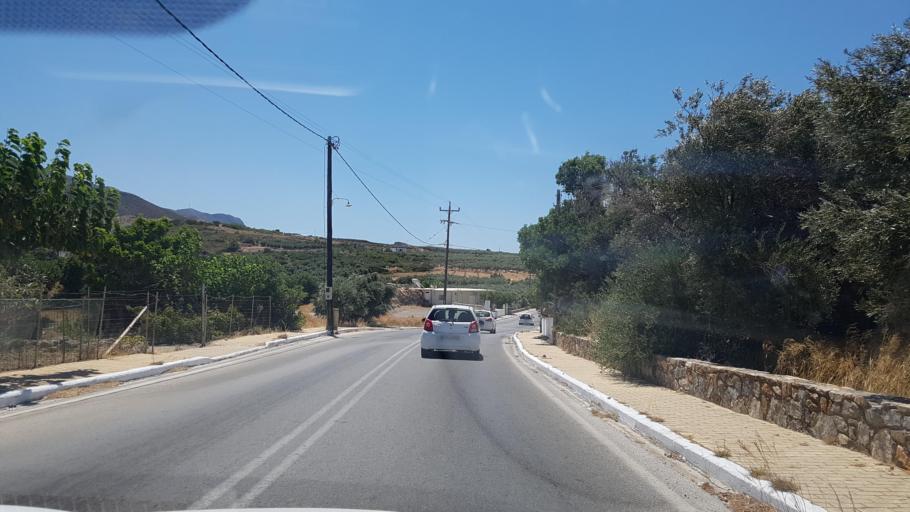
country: GR
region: Crete
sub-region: Nomos Chanias
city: Vryses
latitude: 35.3087
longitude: 23.5371
